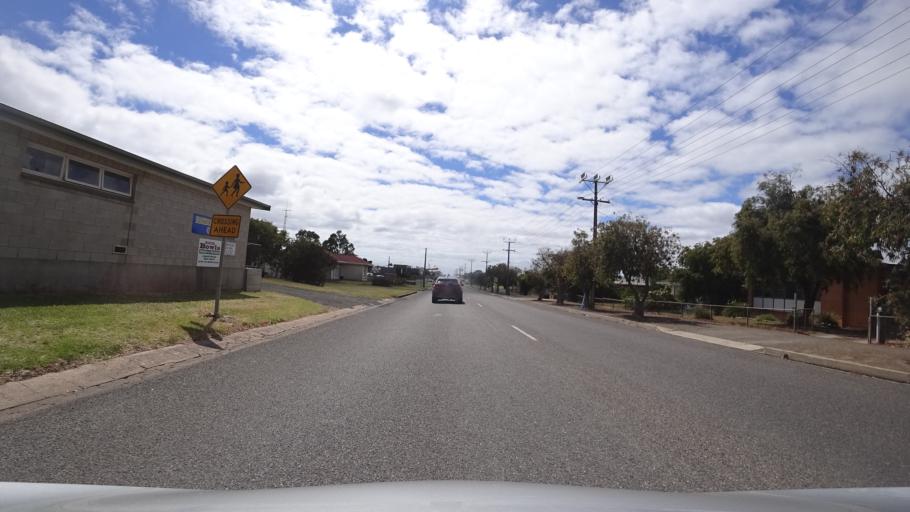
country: AU
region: South Australia
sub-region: Kangaroo Island
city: Kingscote
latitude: -35.6527
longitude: 137.6326
